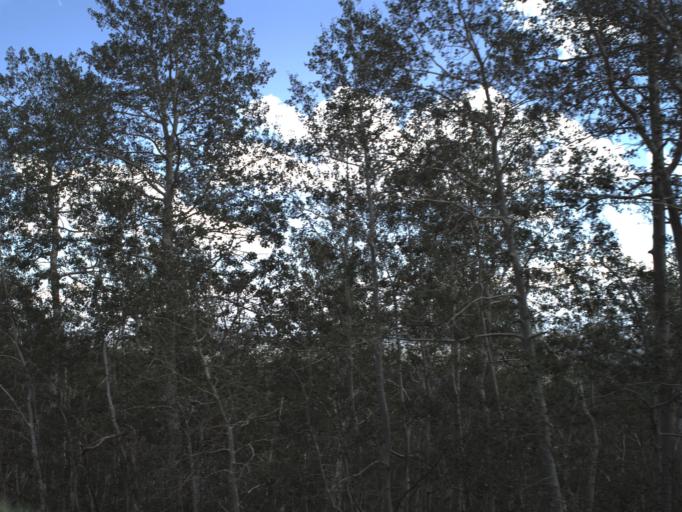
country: US
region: Utah
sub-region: Weber County
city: Wolf Creek
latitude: 41.4504
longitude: -111.5018
